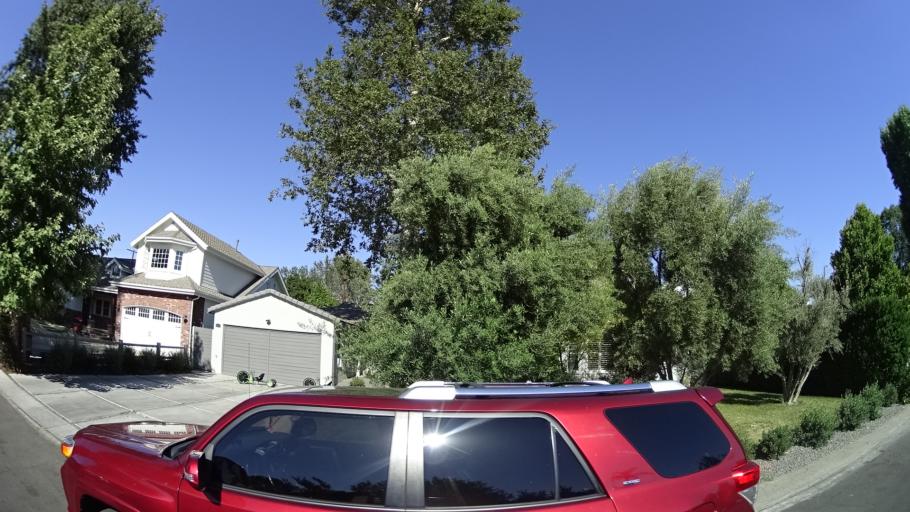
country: US
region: California
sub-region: Los Angeles County
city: North Hollywood
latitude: 34.1525
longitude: -118.3910
